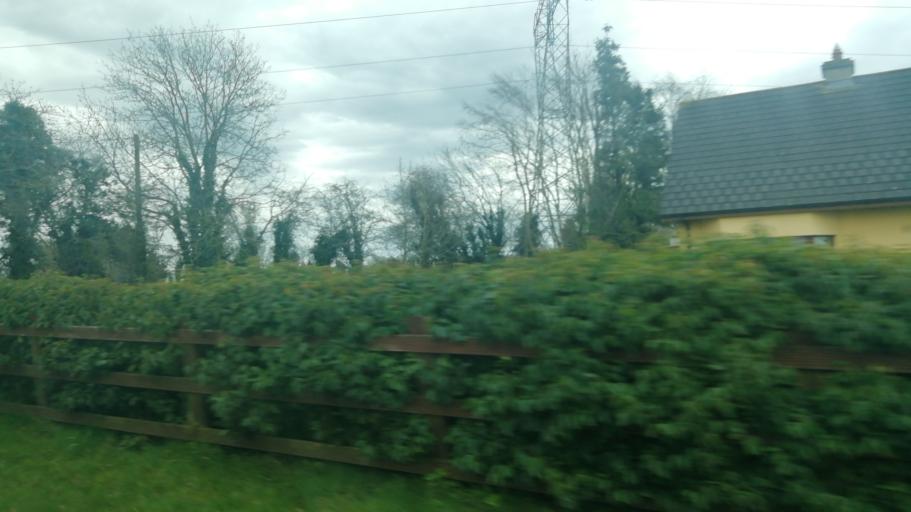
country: IE
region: Leinster
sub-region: Kildare
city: Prosperous
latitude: 53.3029
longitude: -6.7309
